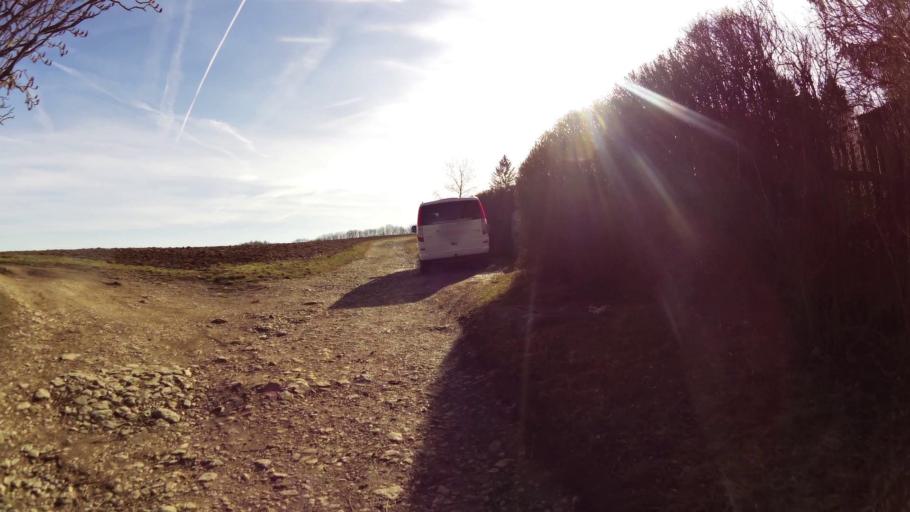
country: DE
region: Thuringia
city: Weimar
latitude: 50.9598
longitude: 11.3289
